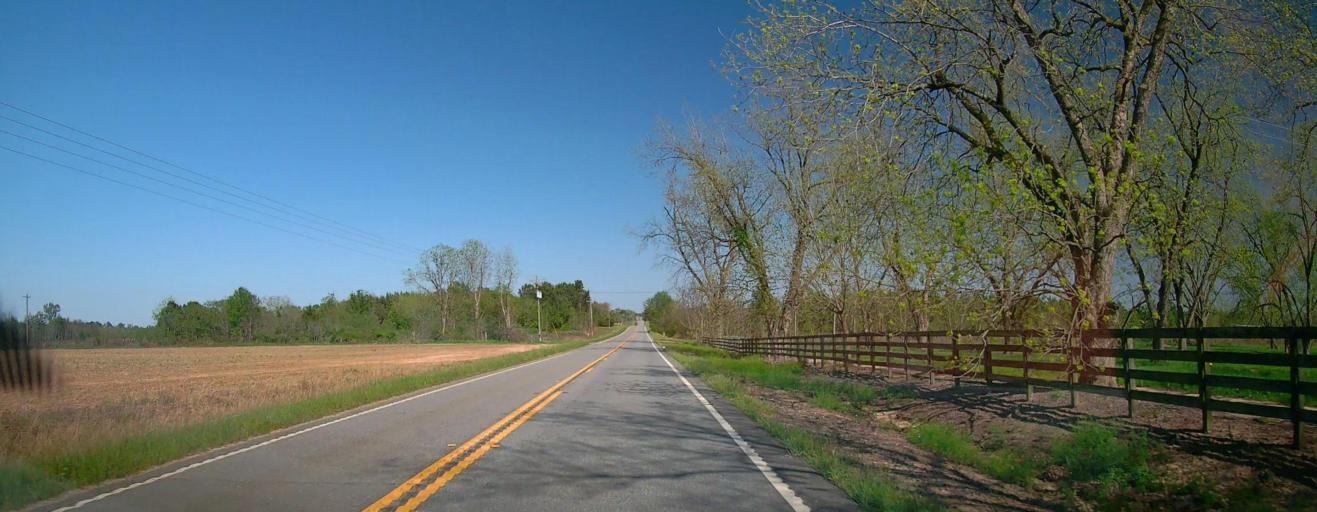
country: US
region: Georgia
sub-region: Dooly County
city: Unadilla
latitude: 32.2602
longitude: -83.7020
